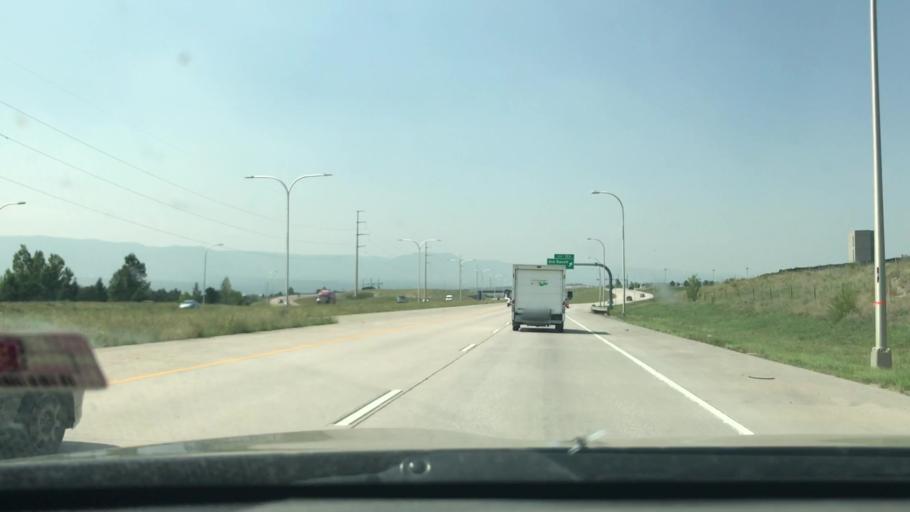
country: US
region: Colorado
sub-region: El Paso County
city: Black Forest
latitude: 38.9808
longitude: -104.7590
